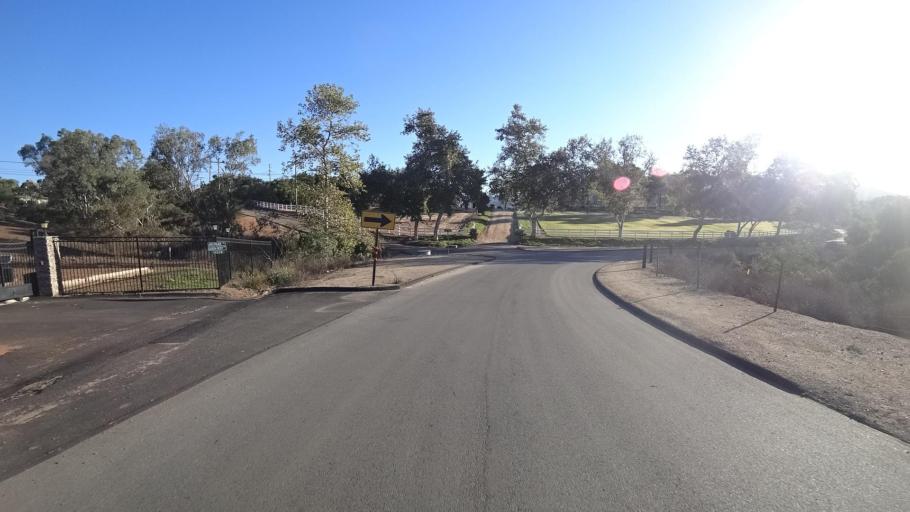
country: US
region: California
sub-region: San Diego County
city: Jamul
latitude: 32.7134
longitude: -116.8642
